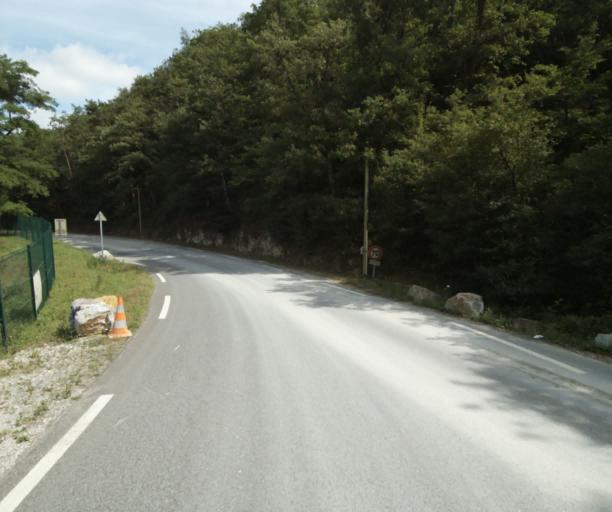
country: FR
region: Midi-Pyrenees
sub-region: Departement du Tarn
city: Soreze
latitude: 43.4574
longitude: 2.1081
